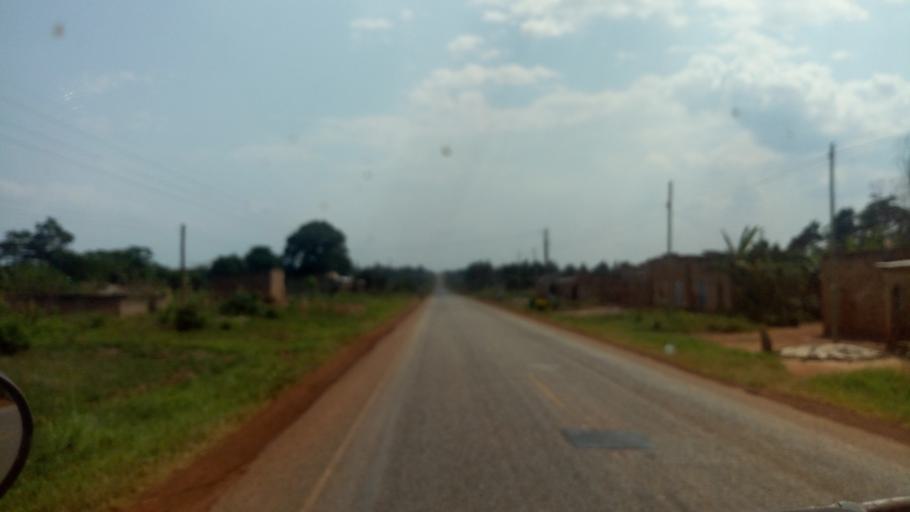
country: UG
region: Northern Region
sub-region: Oyam District
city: Oyam
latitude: 2.2184
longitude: 32.4000
